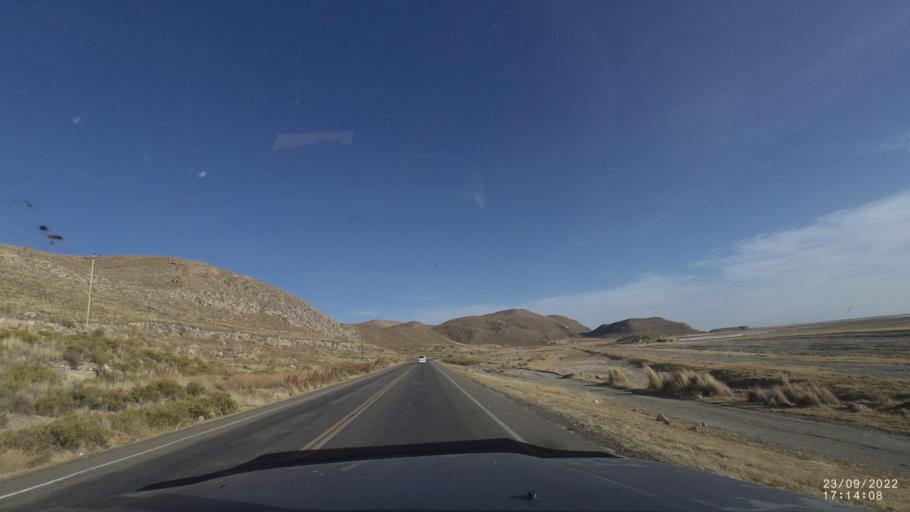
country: BO
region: Oruro
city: Challapata
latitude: -18.7177
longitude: -66.8685
